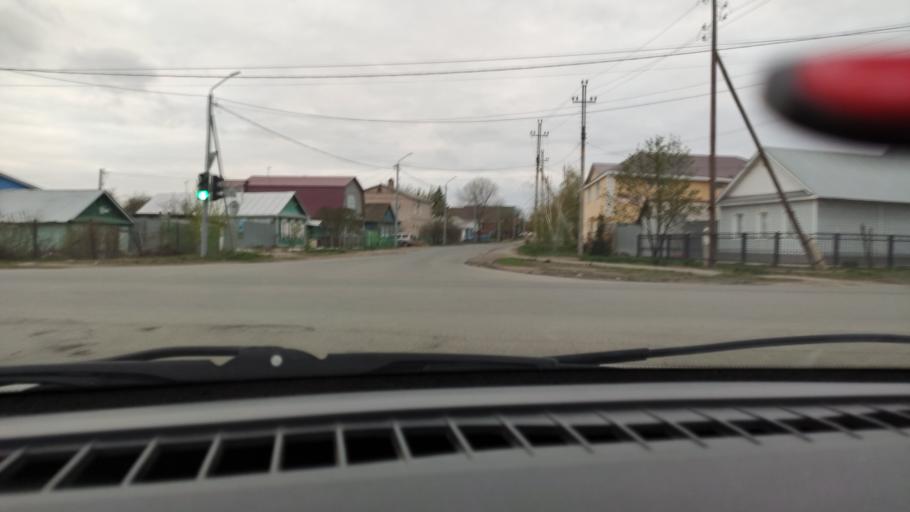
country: RU
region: Orenburg
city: Orenburg
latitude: 51.7796
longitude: 55.1362
